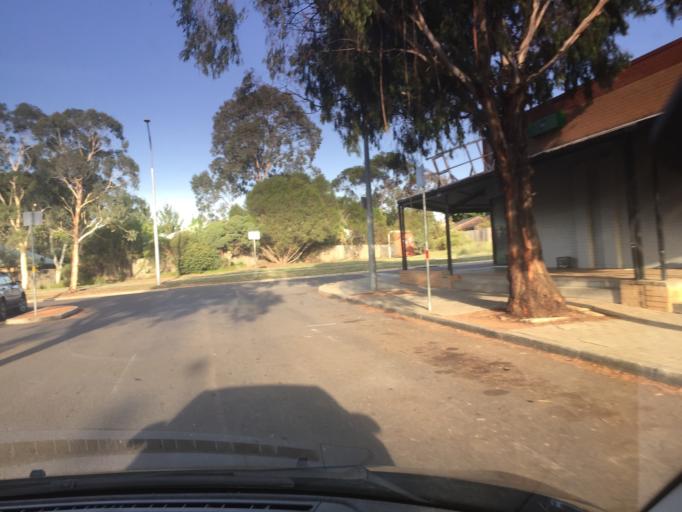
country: AU
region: Australian Capital Territory
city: Kaleen
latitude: -35.2198
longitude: 149.1035
